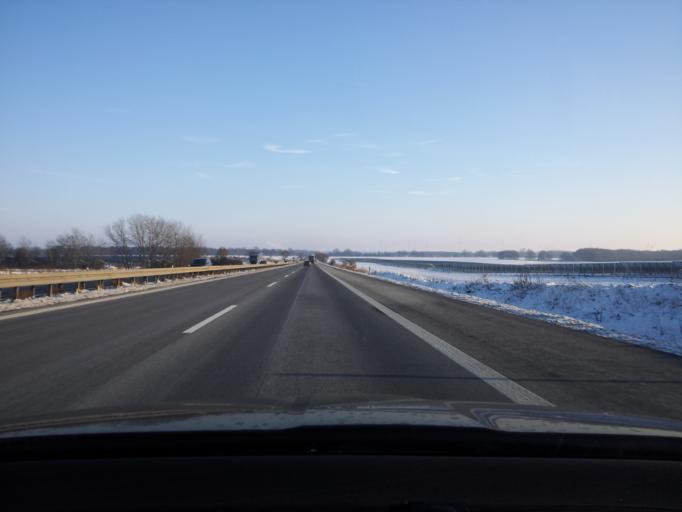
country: DE
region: Brandenburg
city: Gerdshagen
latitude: 53.2153
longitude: 12.2424
